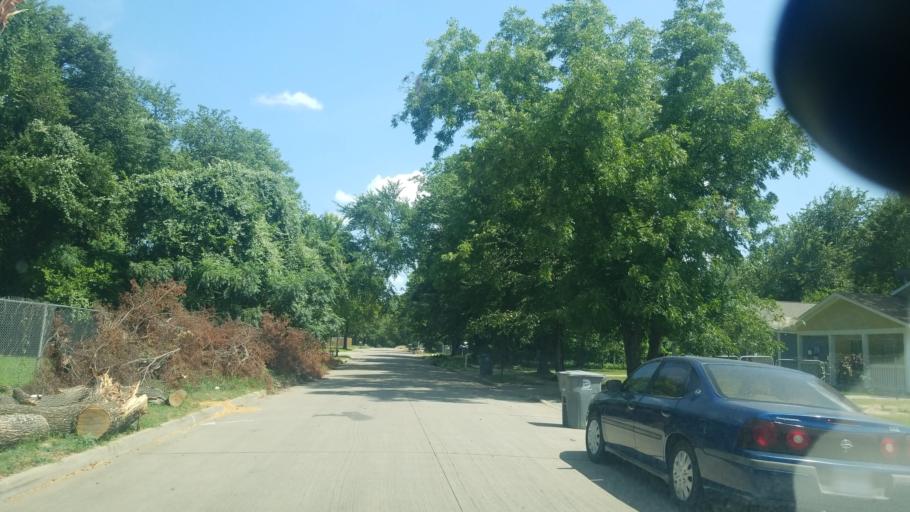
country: US
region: Texas
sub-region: Dallas County
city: Hutchins
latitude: 32.7148
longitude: -96.7454
